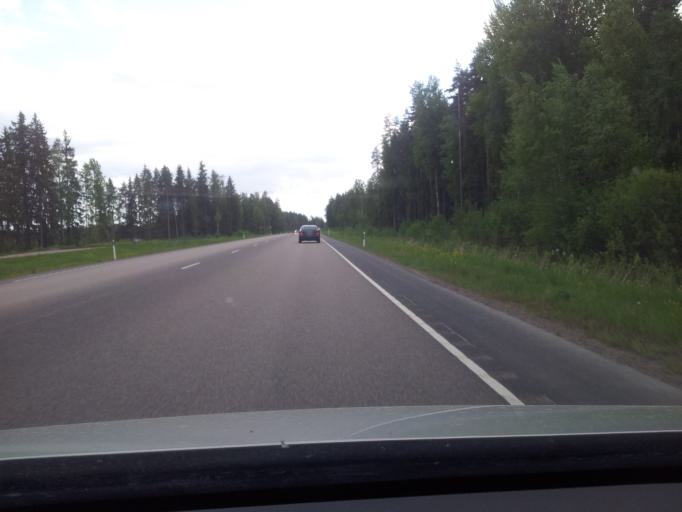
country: FI
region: Kymenlaakso
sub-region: Kouvola
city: Elimaeki
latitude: 60.8368
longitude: 26.5409
